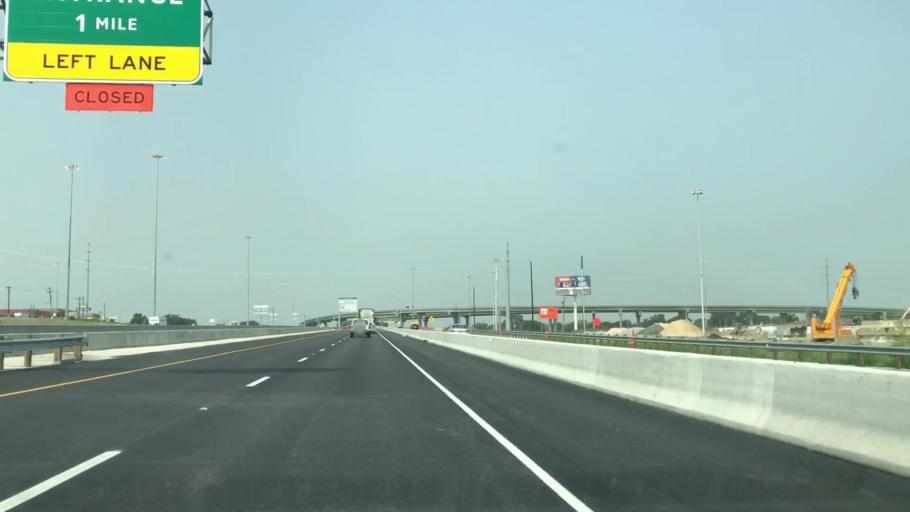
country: US
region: Texas
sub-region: Dallas County
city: Irving
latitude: 32.8376
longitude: -96.9074
